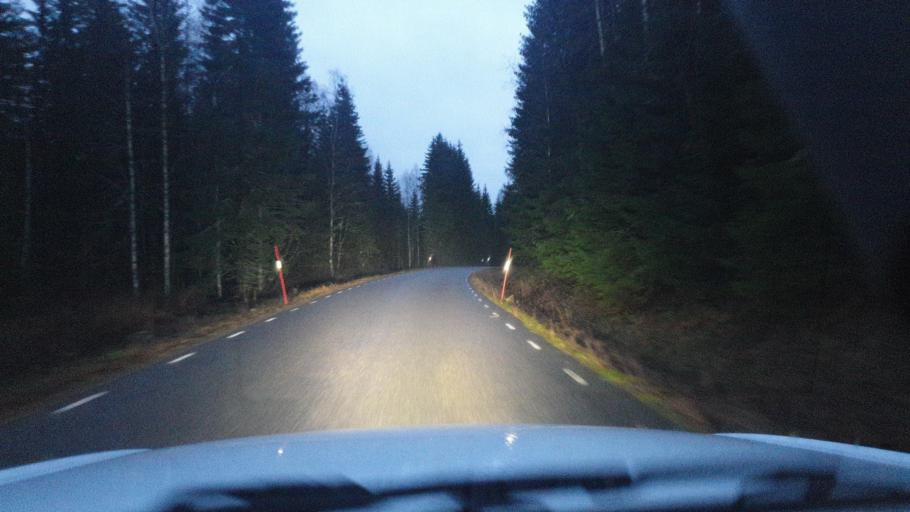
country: SE
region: Vaermland
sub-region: Torsby Kommun
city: Torsby
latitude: 60.0103
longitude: 12.6835
